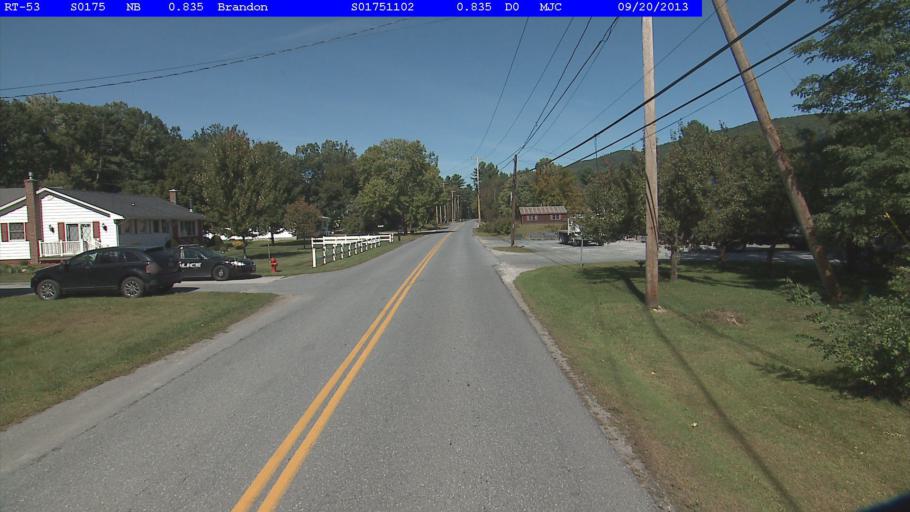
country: US
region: Vermont
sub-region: Rutland County
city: Brandon
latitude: 43.8388
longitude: -73.0563
